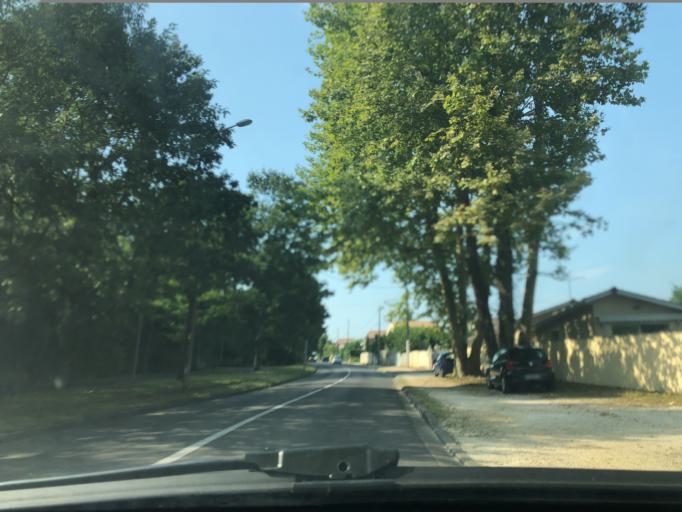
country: FR
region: Aquitaine
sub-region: Departement de la Gironde
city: Merignac
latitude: 44.8266
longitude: -0.6378
